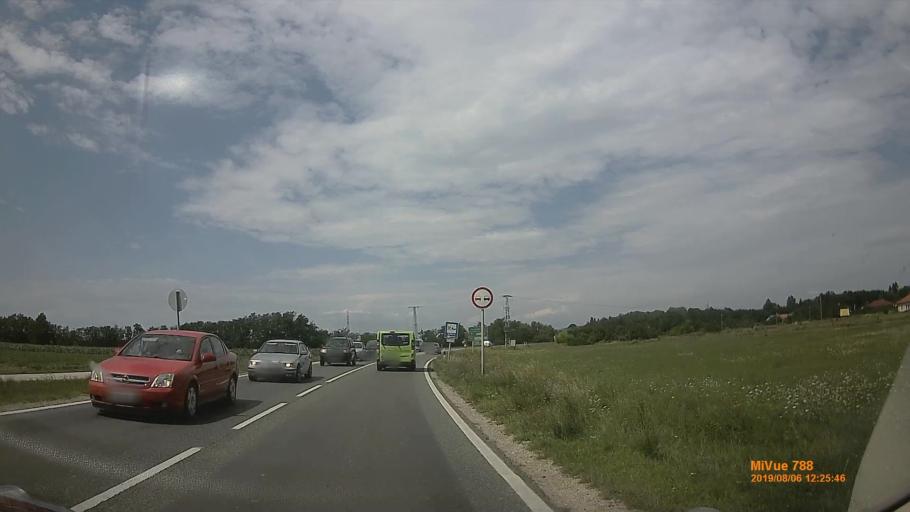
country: HU
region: Vas
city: Taplanszentkereszt
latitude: 47.1982
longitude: 16.6824
